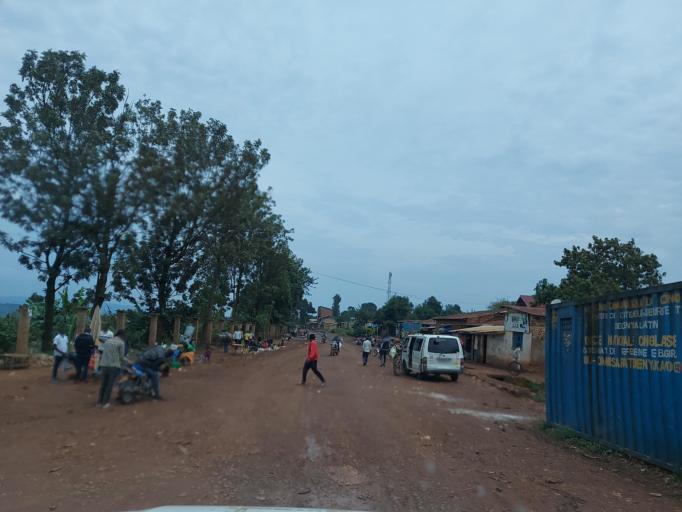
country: CD
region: South Kivu
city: Bukavu
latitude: -2.4829
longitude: 28.8195
